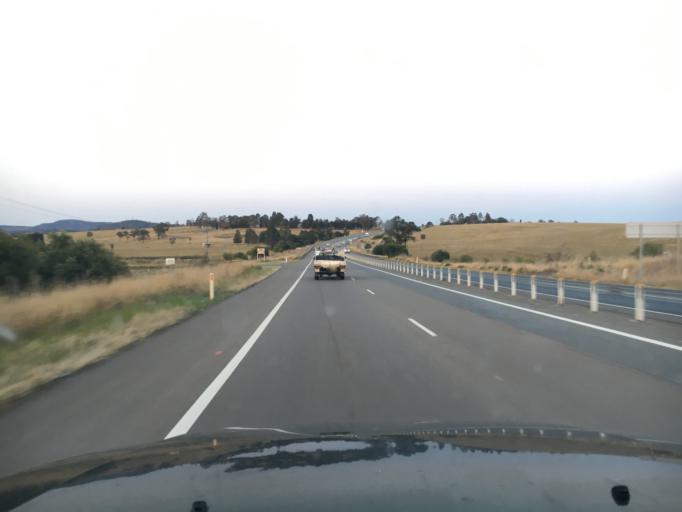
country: AU
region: New South Wales
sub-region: Cessnock
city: Greta
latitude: -32.7081
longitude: 151.4274
